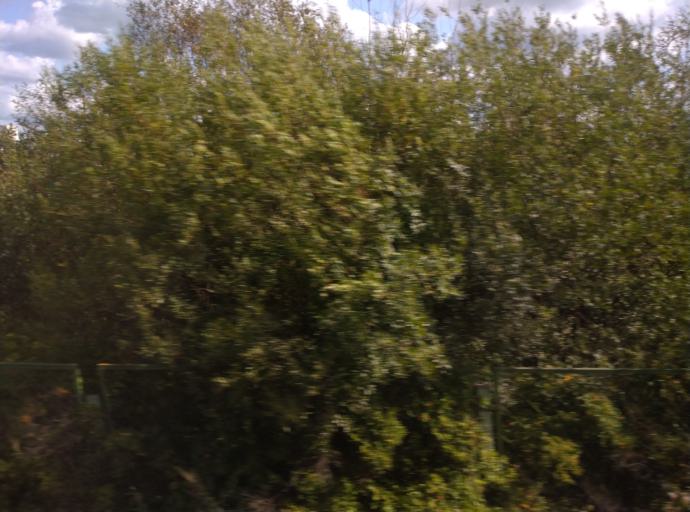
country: RU
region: St.-Petersburg
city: Kolpino
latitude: 59.7345
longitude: 30.6331
